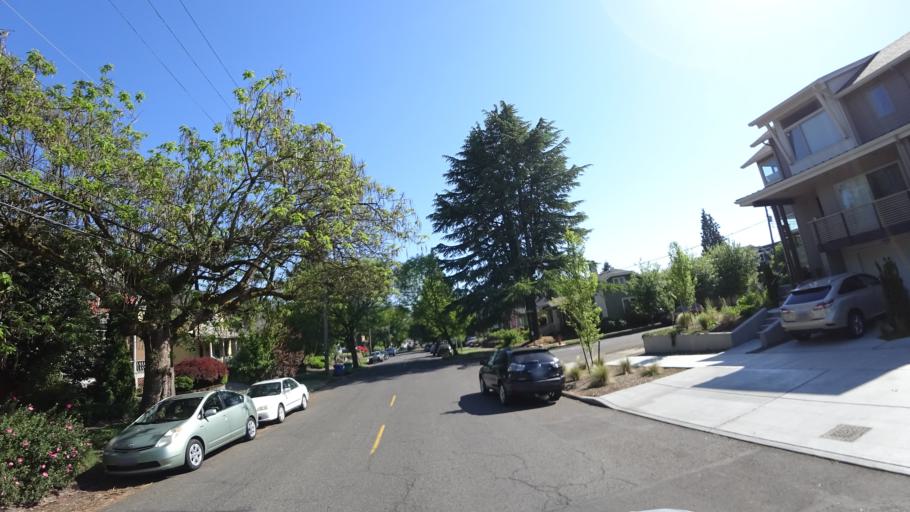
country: US
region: Oregon
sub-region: Multnomah County
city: Portland
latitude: 45.5389
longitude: -122.6586
